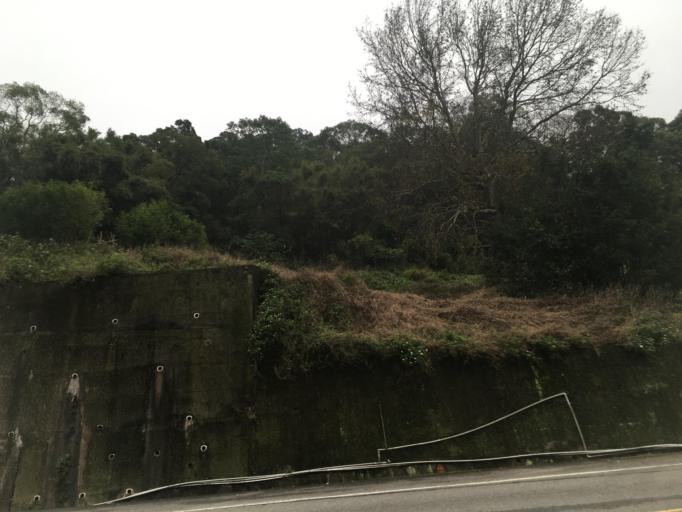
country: TW
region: Taiwan
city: Fengyuan
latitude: 24.4114
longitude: 120.7393
